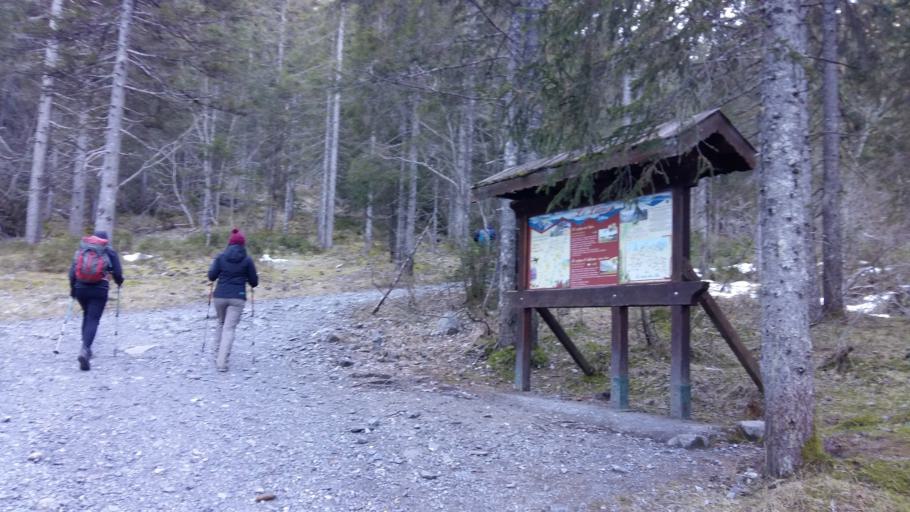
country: FR
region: Rhone-Alpes
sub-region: Departement de la Haute-Savoie
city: Samoens
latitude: 46.0198
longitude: 6.7663
